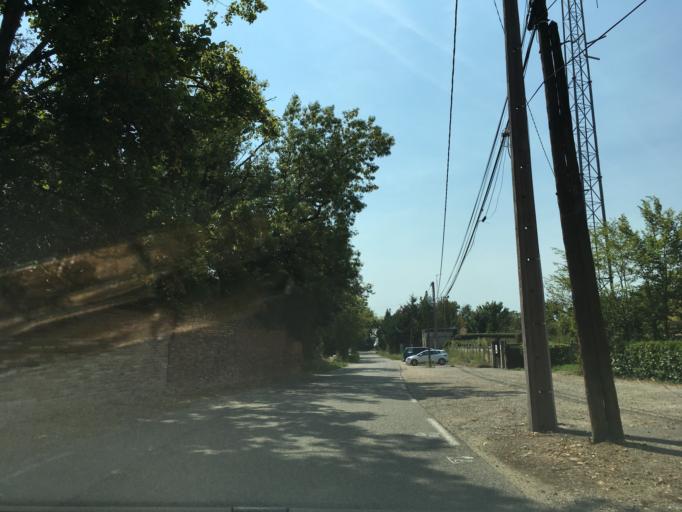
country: FR
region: Midi-Pyrenees
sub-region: Departement du Tarn-et-Garonne
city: Saint-Nauphary
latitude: 43.9914
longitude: 1.4218
